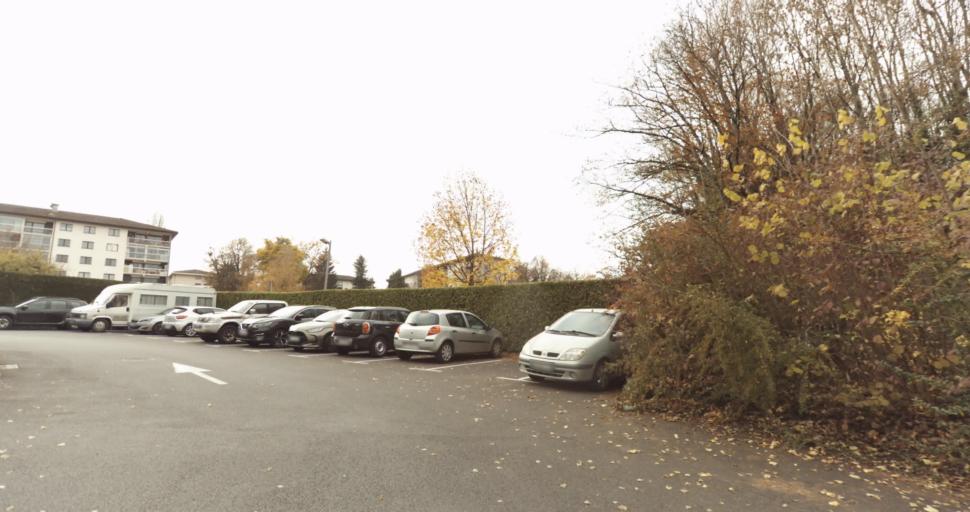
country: FR
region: Rhone-Alpes
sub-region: Departement de la Haute-Savoie
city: Annecy
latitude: 45.8964
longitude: 6.1093
